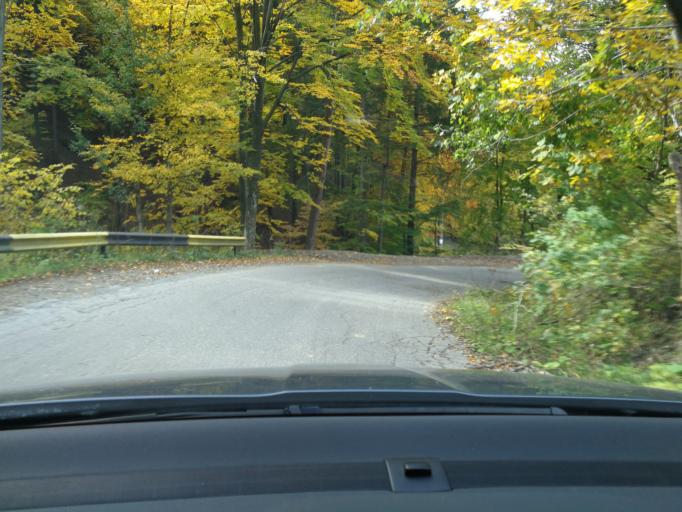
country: RO
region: Prahova
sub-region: Comuna Brebu
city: Pietriceaua
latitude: 45.2052
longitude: 25.7983
